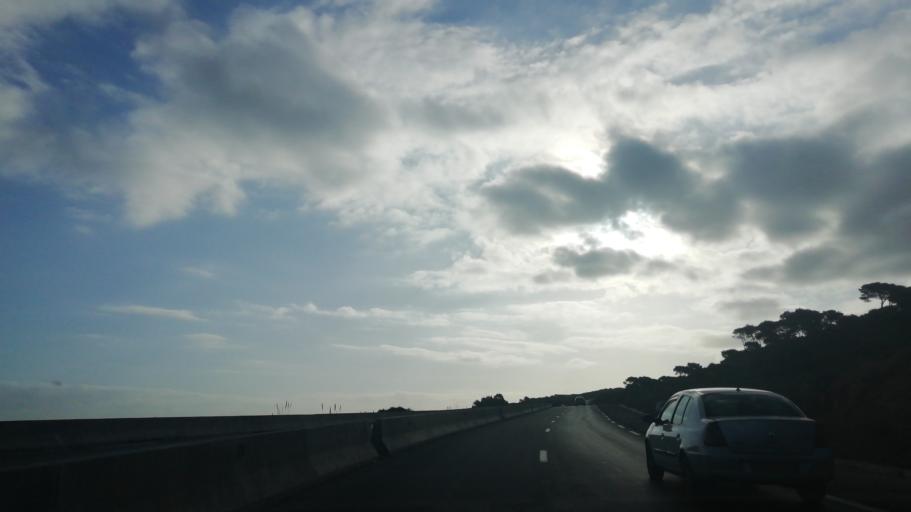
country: DZ
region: Mostaganem
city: Mostaganem
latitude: 36.1122
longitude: 0.2556
